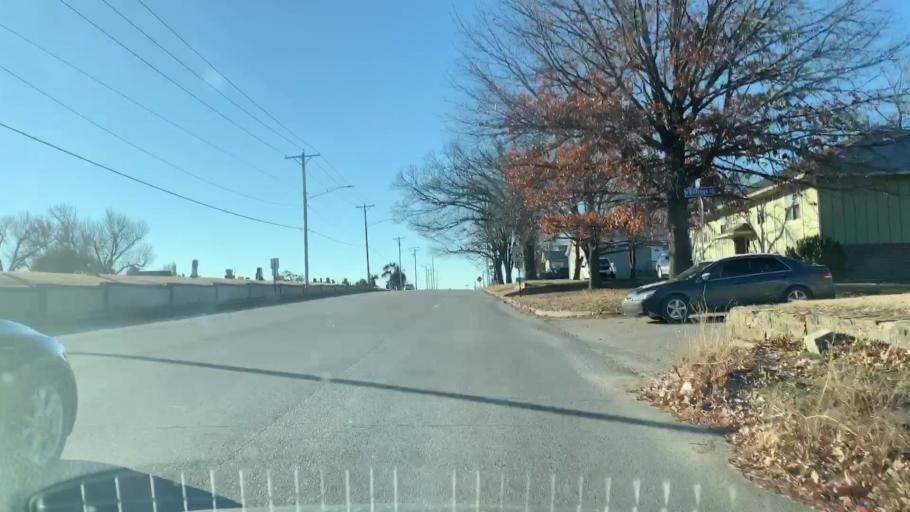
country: US
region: Kansas
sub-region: Crawford County
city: Pittsburg
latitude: 37.3853
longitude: -94.7053
